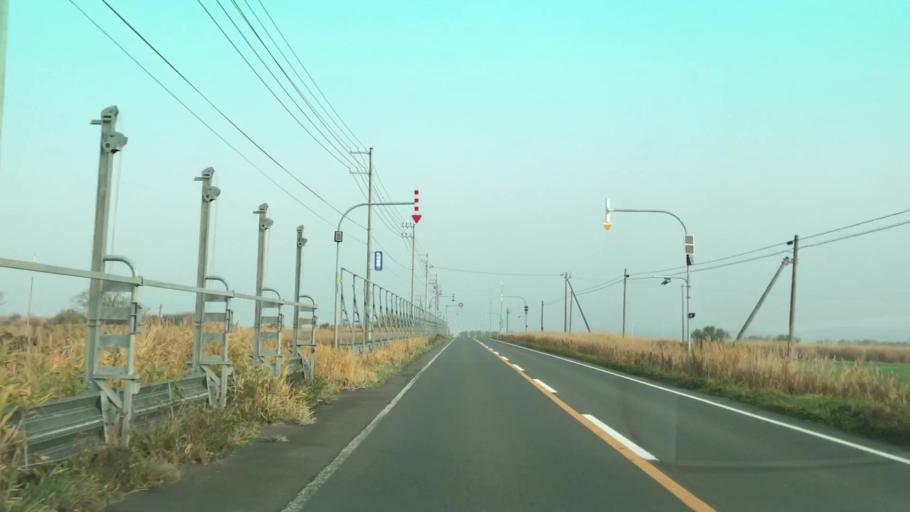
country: JP
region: Hokkaido
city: Ishikari
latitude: 43.2989
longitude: 141.4116
